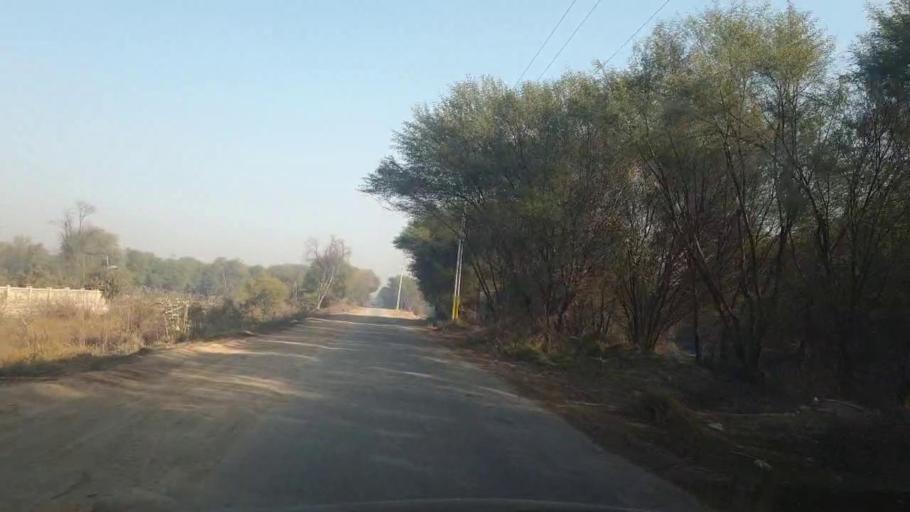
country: PK
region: Sindh
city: Mirpur Mathelo
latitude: 28.0541
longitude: 69.4619
